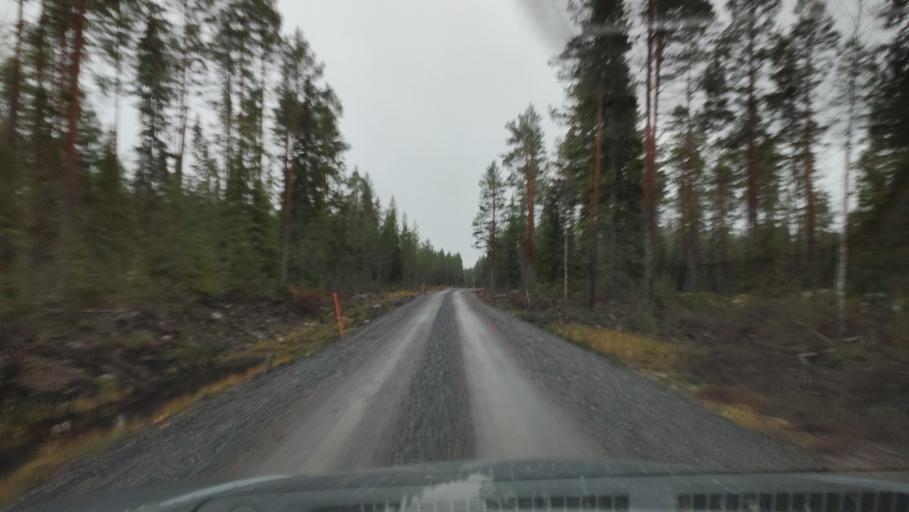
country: FI
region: Southern Ostrobothnia
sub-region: Suupohja
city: Karijoki
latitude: 62.1622
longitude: 21.5901
